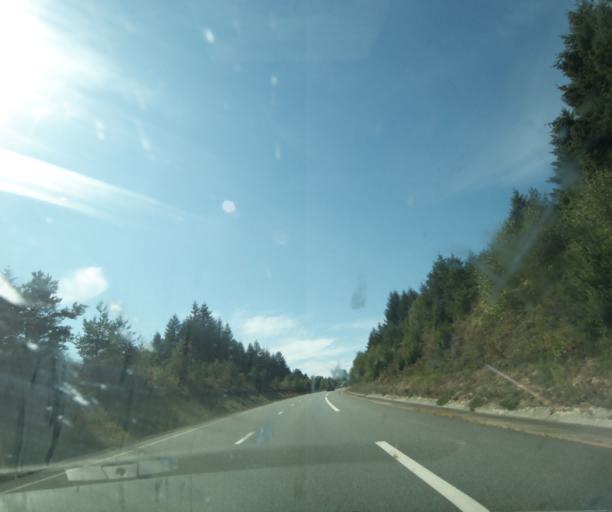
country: FR
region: Limousin
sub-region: Departement de la Correze
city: Correze
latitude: 45.3581
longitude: 1.9397
